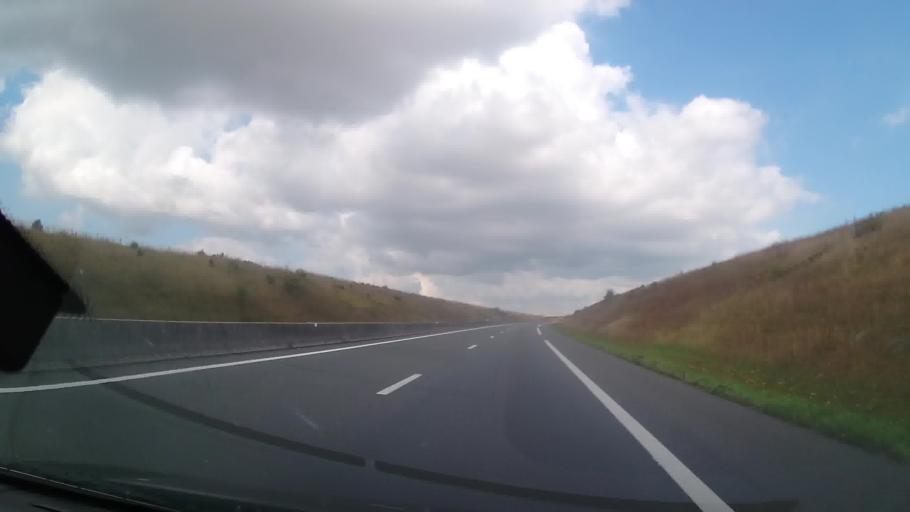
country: FR
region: Nord-Pas-de-Calais
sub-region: Departement du Pas-de-Calais
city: Verton
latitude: 50.3533
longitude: 1.6884
